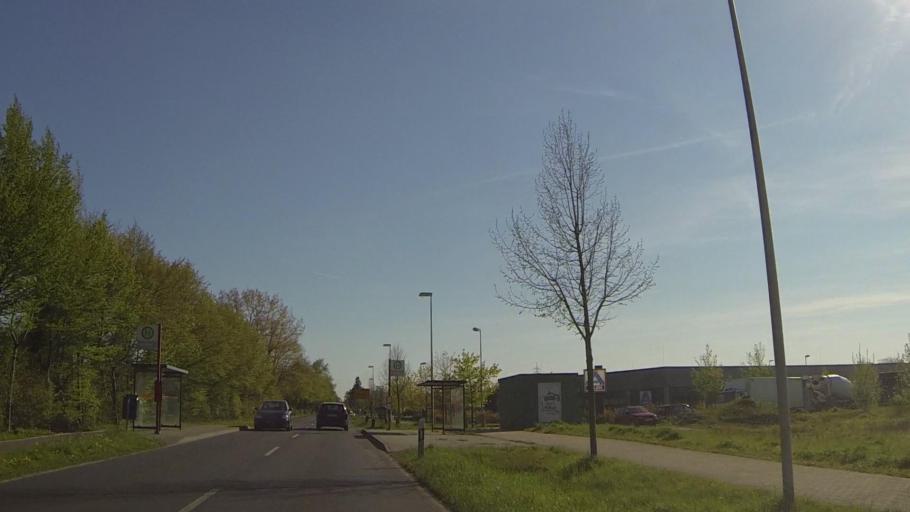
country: DE
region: Schleswig-Holstein
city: Pinneberg
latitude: 53.6473
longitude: 9.7735
